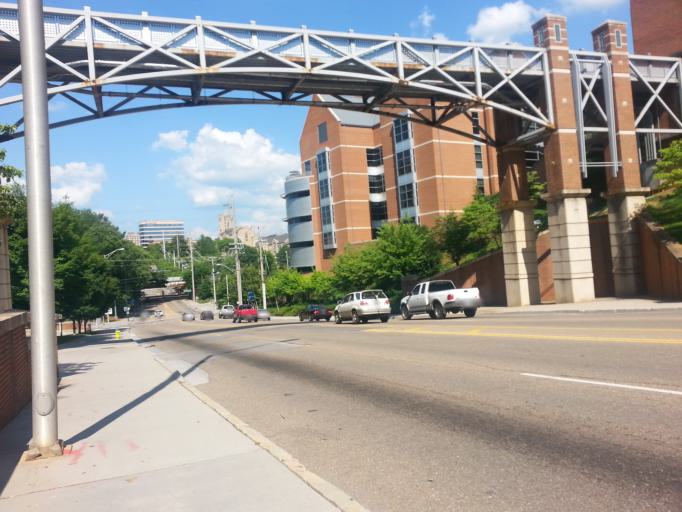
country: US
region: Tennessee
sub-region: Knox County
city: Knoxville
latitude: 35.9590
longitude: -83.9259
